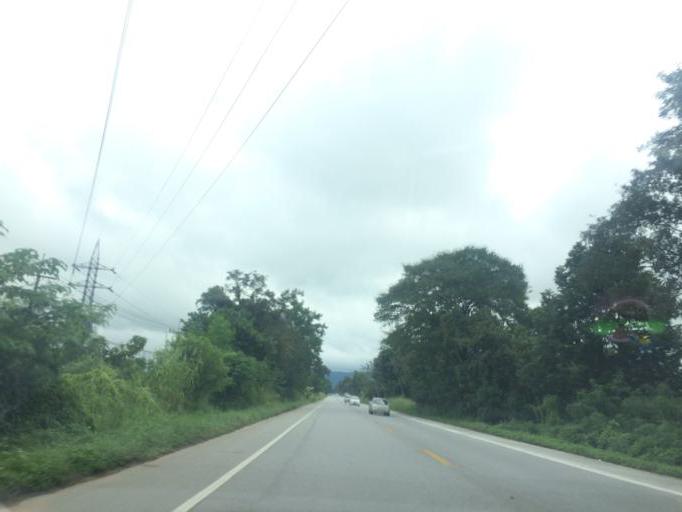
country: TH
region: Chiang Rai
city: Mae Lao
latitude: 19.7461
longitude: 99.6938
